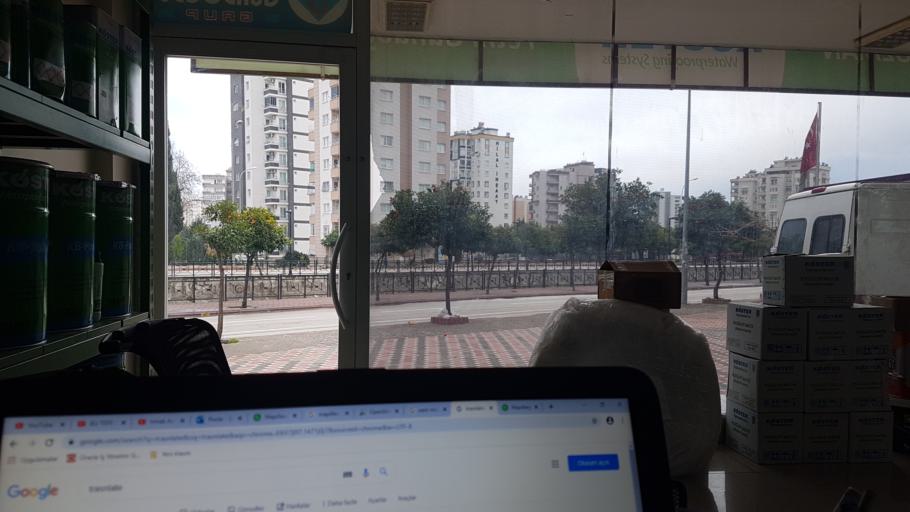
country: TR
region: Adana
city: Seyhan
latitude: 37.0291
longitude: 35.2785
